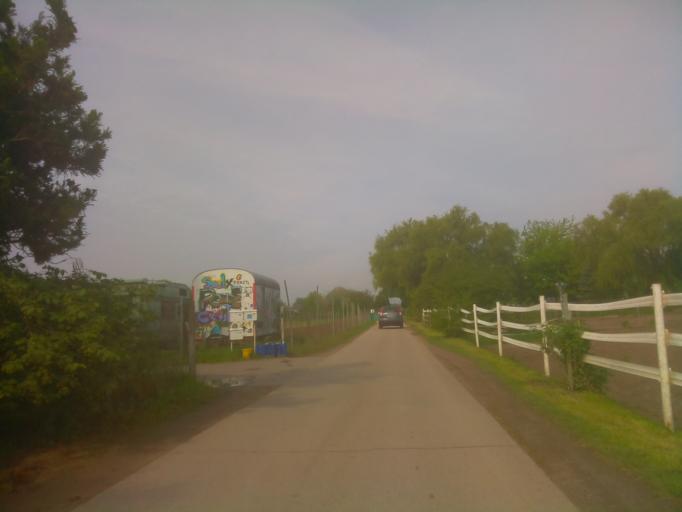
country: DE
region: Baden-Wuerttemberg
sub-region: Karlsruhe Region
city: Heddesheim
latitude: 49.4905
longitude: 8.6072
